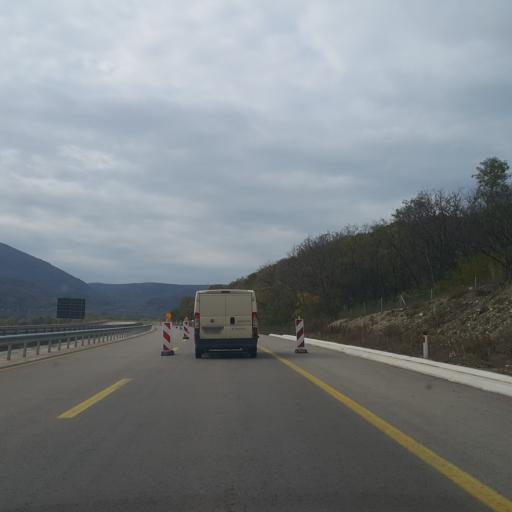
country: RS
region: Central Serbia
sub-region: Pirotski Okrug
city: Bela Palanka
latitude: 43.2367
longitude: 22.3029
